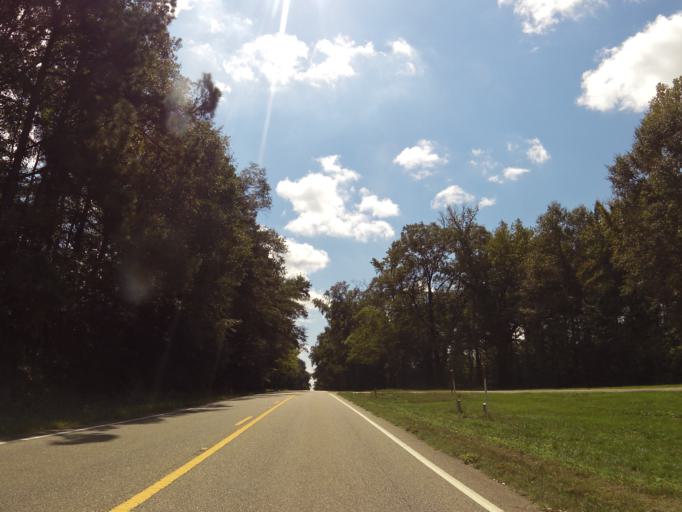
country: US
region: Alabama
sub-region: Dallas County
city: Selma
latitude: 32.4850
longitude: -87.0928
